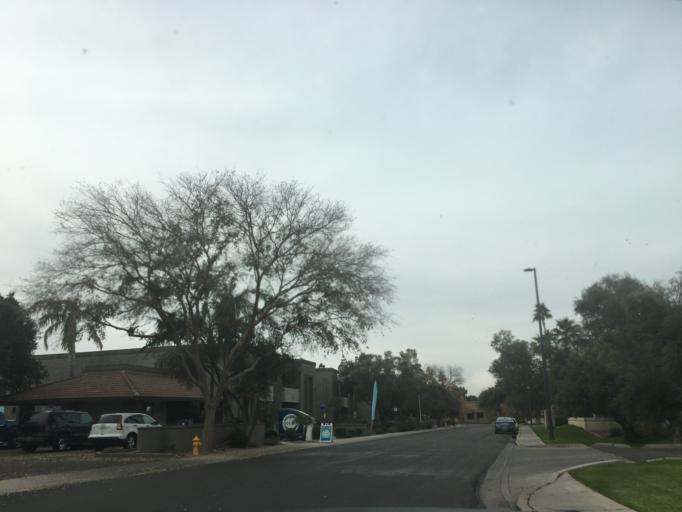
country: US
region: Arizona
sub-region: Maricopa County
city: Gilbert
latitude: 33.3606
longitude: -111.7878
